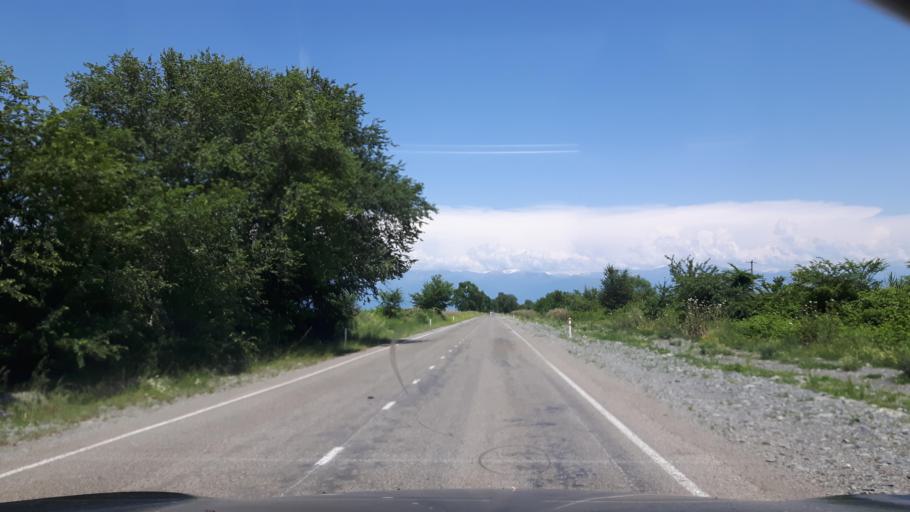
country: GE
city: Tsnori
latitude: 41.6287
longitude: 46.0179
